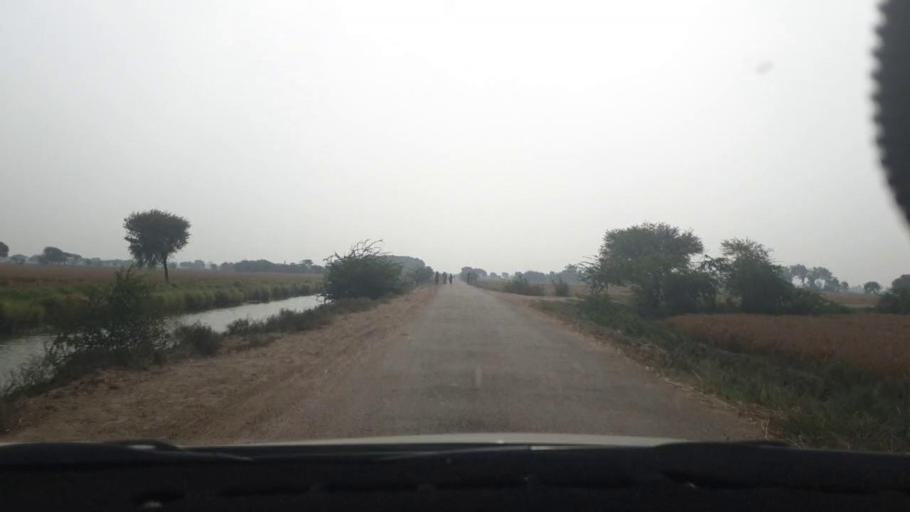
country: PK
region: Sindh
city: Tando Muhammad Khan
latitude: 25.0615
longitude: 68.5435
